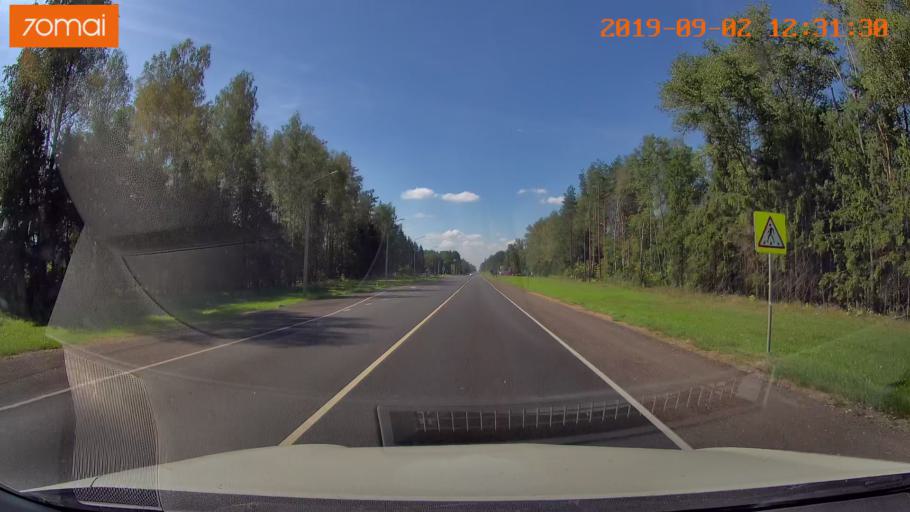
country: RU
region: Smolensk
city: Shumyachi
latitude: 53.8240
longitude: 32.4483
